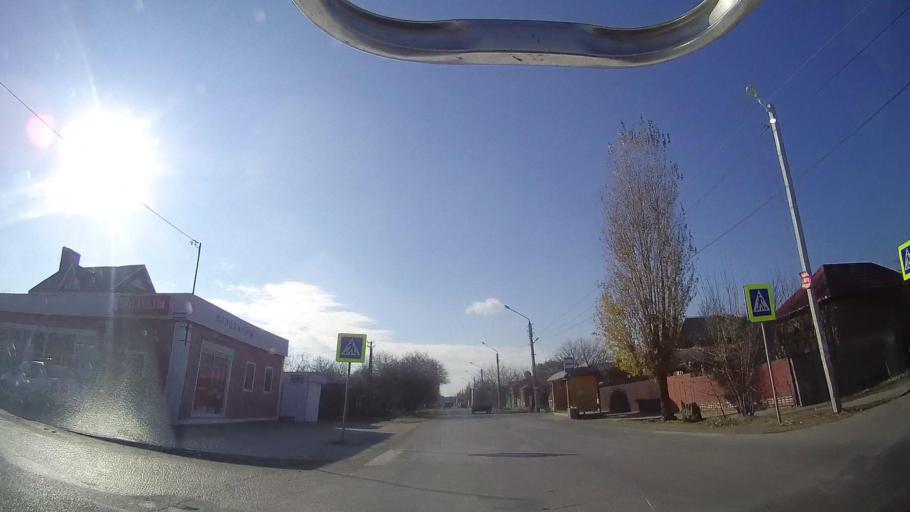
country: RU
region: Rostov
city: Bataysk
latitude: 47.1325
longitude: 39.6996
